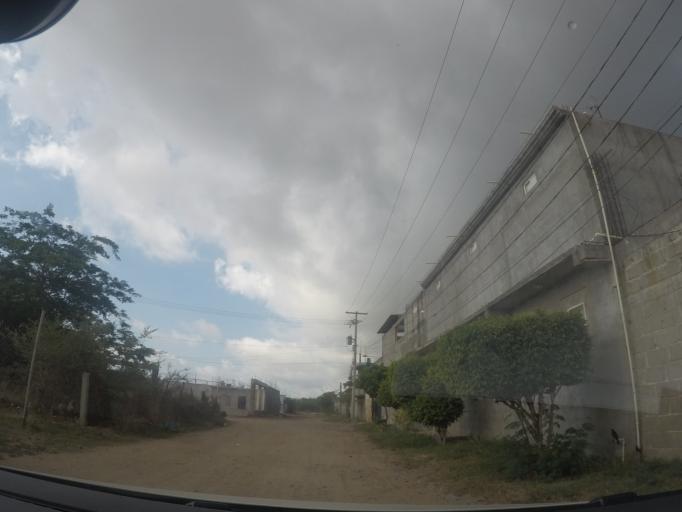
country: MX
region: Oaxaca
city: Juchitan de Zaragoza
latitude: 16.4286
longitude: -95.0343
